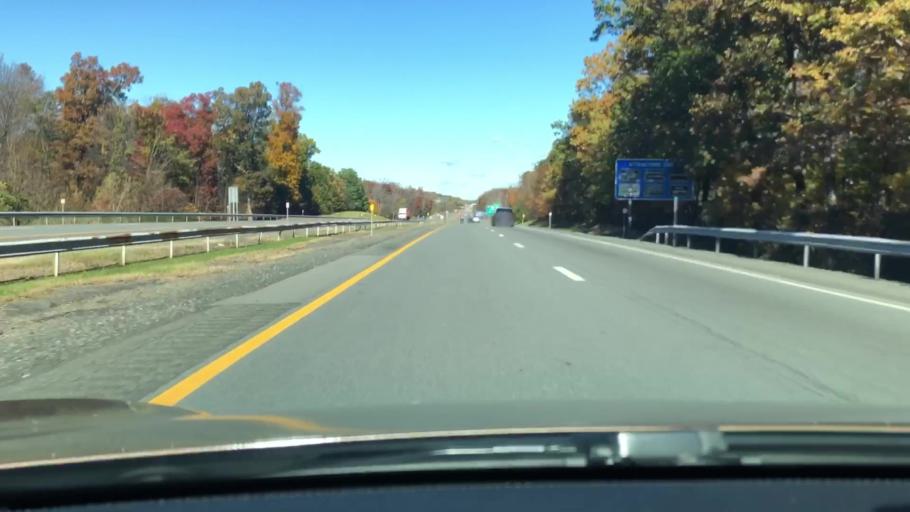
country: US
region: New York
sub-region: Orange County
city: Vails Gate
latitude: 41.4913
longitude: -74.0786
